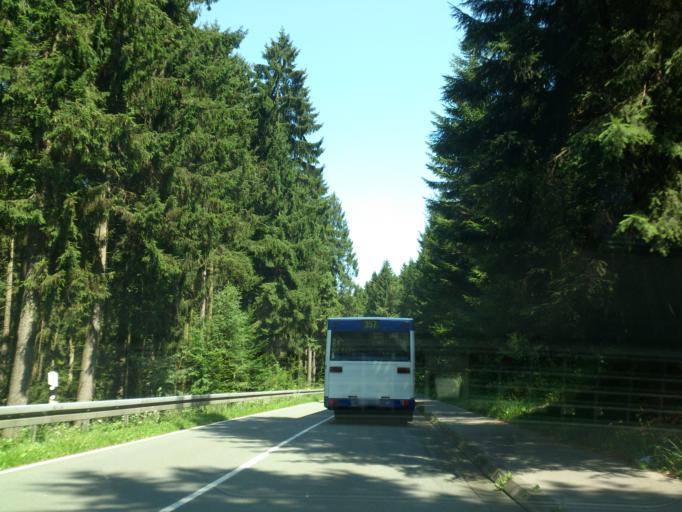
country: DE
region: North Rhine-Westphalia
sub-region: Regierungsbezirk Detmold
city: Horn
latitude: 51.8574
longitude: 8.9276
